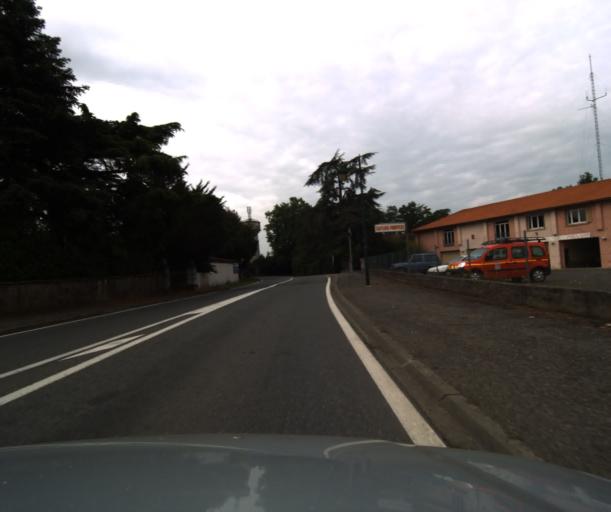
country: FR
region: Midi-Pyrenees
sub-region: Departement du Gers
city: Mielan
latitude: 43.4268
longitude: 0.3069
